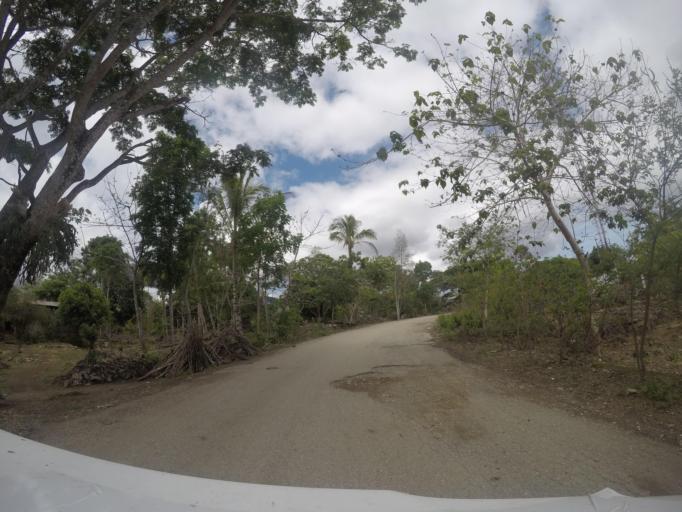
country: TL
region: Baucau
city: Baucau
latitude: -8.4681
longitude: 126.4332
